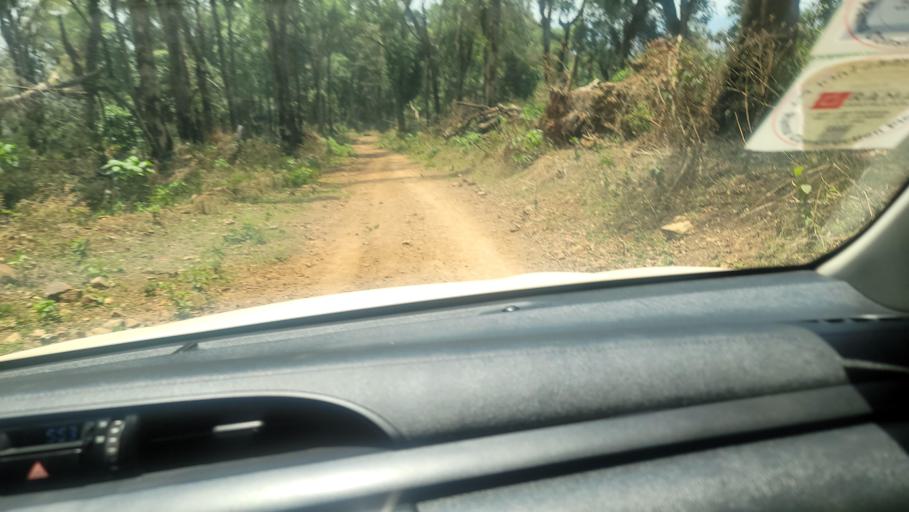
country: ET
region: Southern Nations, Nationalities, and People's Region
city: Bonga
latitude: 7.5403
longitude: 36.1811
